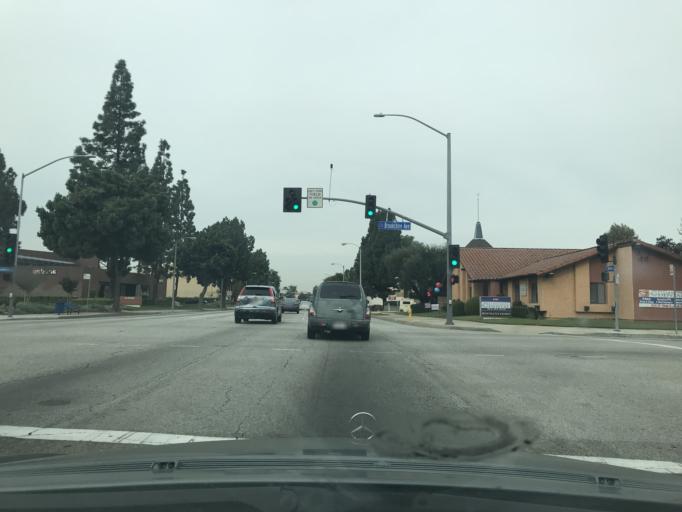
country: US
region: California
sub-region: Los Angeles County
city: Downey
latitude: 33.9498
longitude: -118.1216
